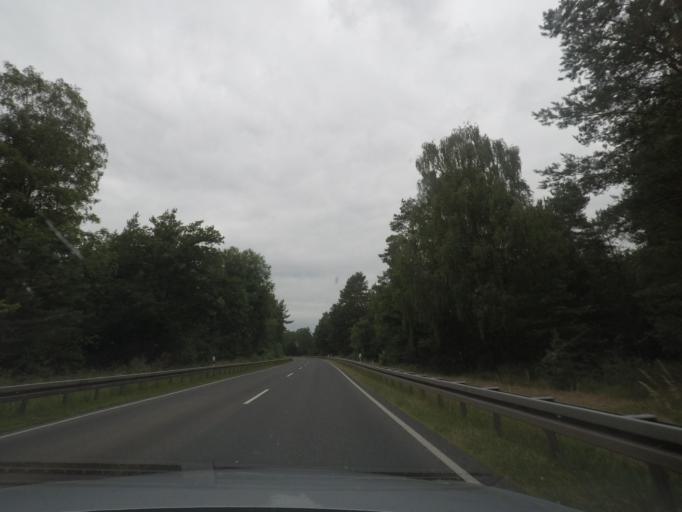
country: DE
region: Saxony-Anhalt
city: Colbitz
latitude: 52.3495
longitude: 11.5696
